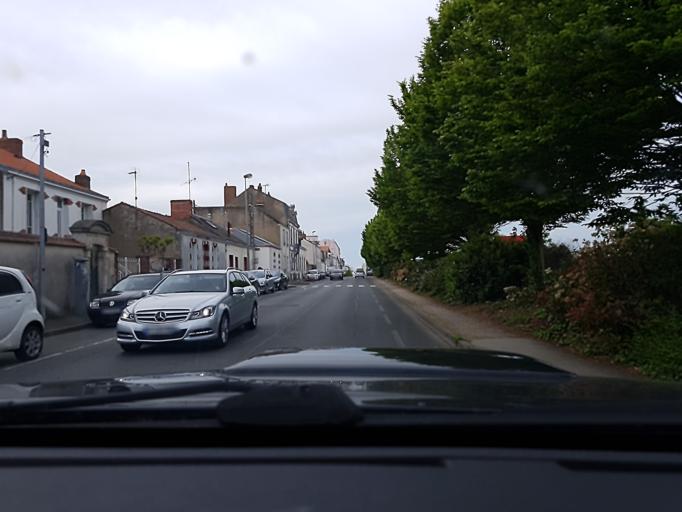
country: FR
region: Pays de la Loire
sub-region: Departement de la Vendee
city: La Roche-sur-Yon
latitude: 46.6755
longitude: -1.4352
